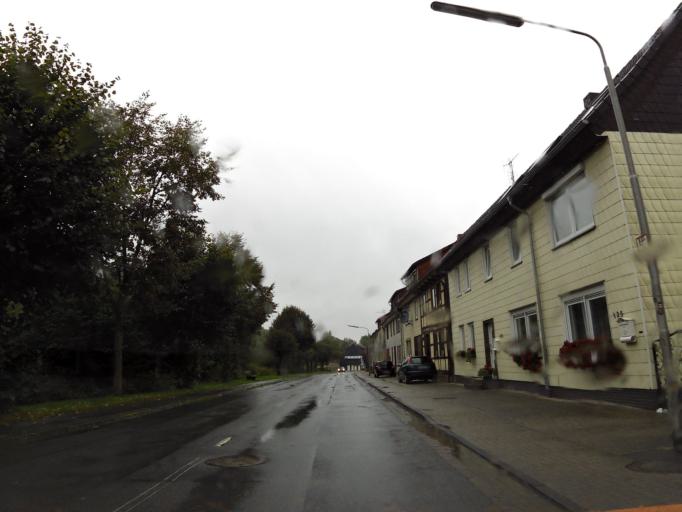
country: DE
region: Lower Saxony
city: Herzberg am Harz
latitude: 51.6265
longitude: 10.3884
